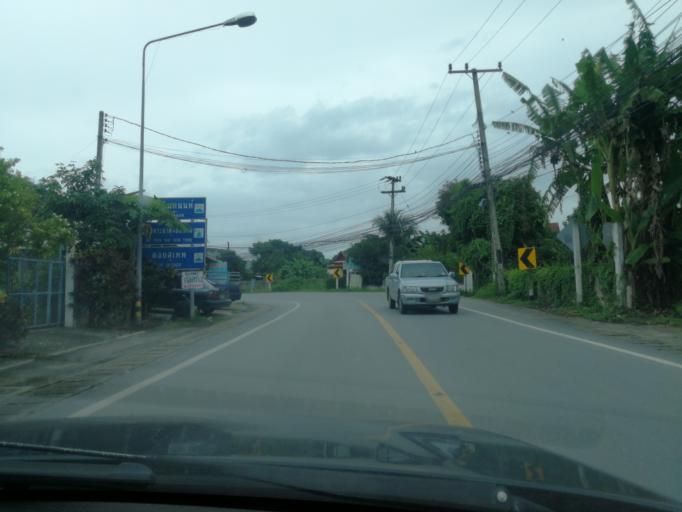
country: TH
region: Chiang Mai
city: San Pa Tong
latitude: 18.6311
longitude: 98.8981
